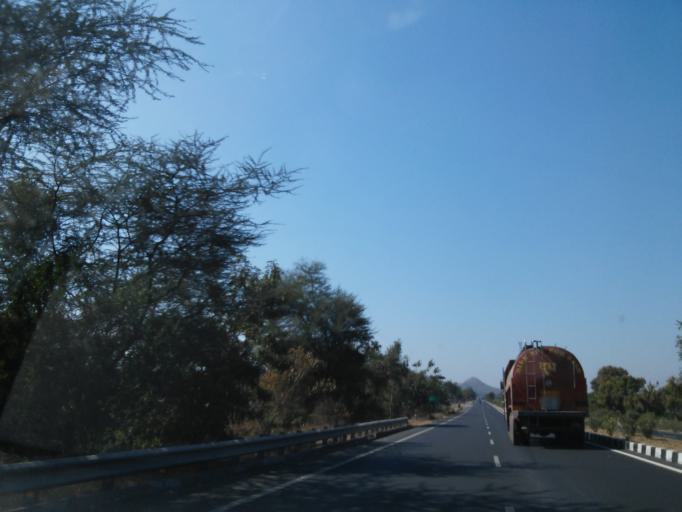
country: IN
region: Gujarat
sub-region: Sabar Kantha
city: Modasa
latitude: 23.6216
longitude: 73.2888
